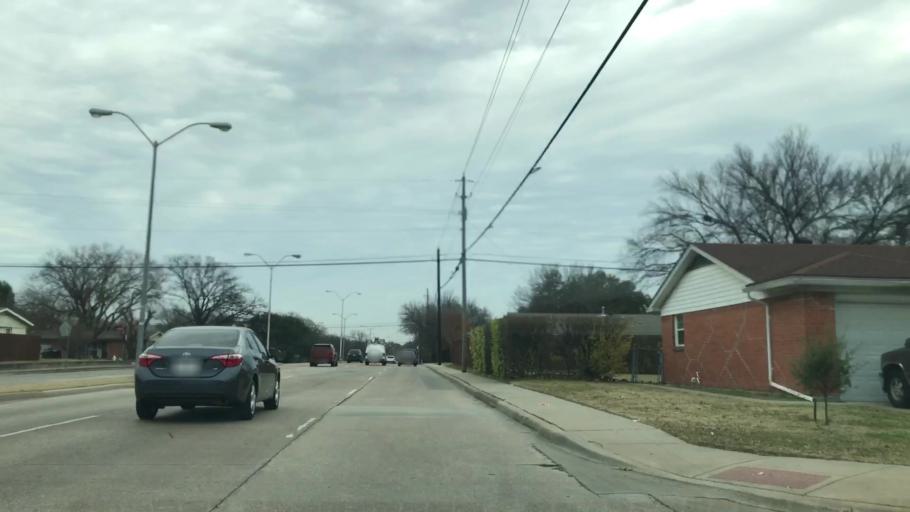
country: US
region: Texas
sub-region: Dallas County
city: Farmers Branch
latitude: 32.9330
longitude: -96.8874
